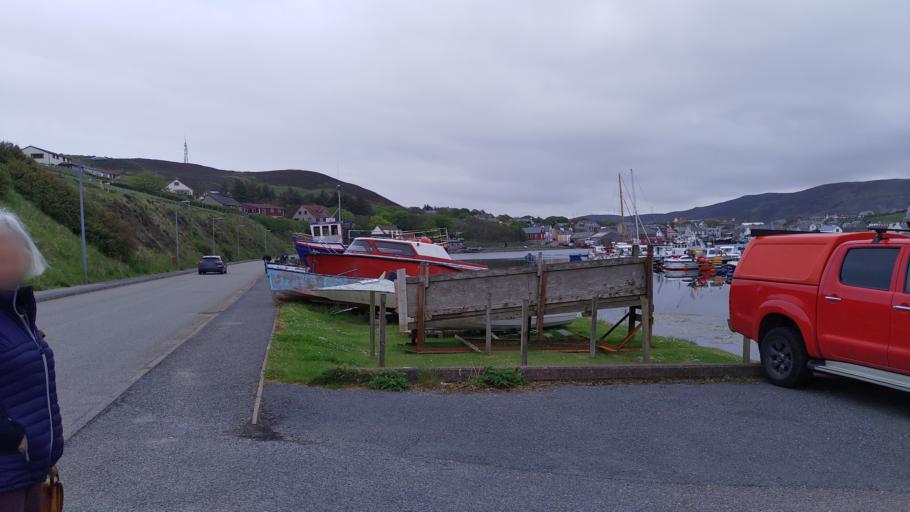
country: GB
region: Scotland
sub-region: Shetland Islands
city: Lerwick
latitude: 60.1343
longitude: -1.2858
